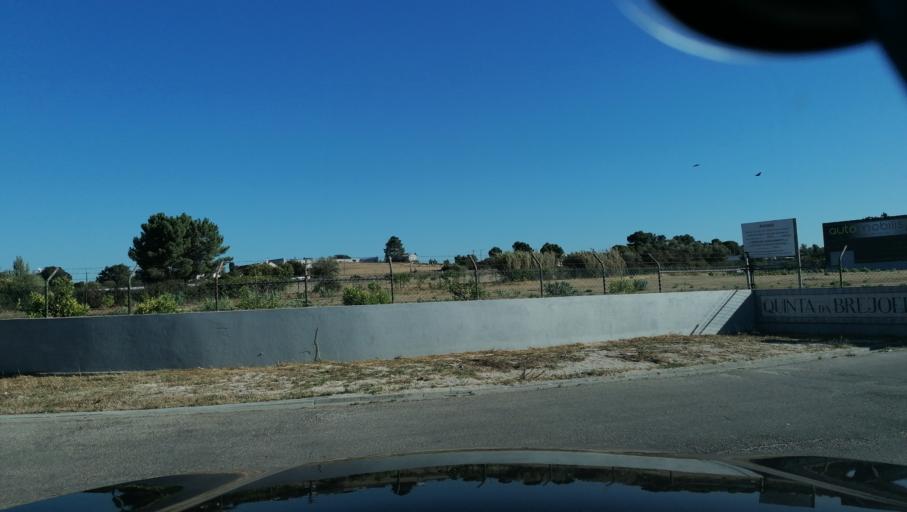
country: PT
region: Setubal
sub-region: Moita
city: Moita
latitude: 38.6371
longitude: -8.9743
